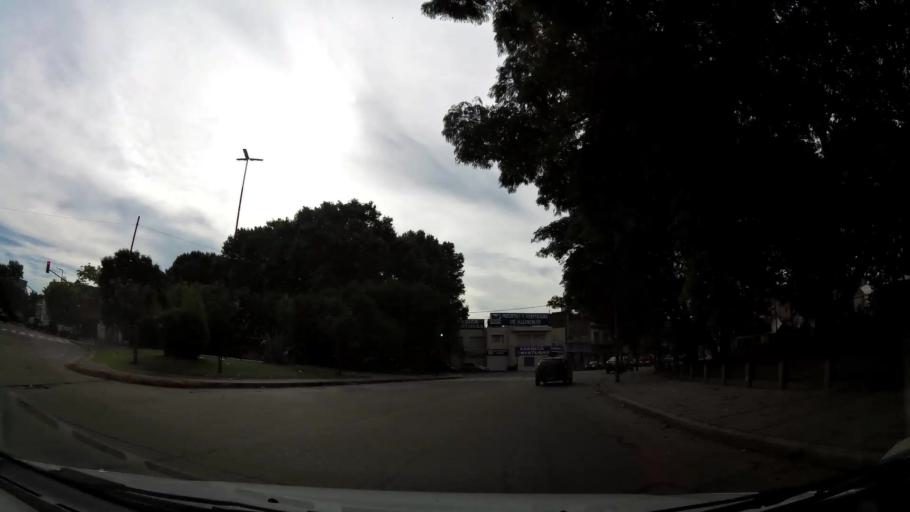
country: AR
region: Buenos Aires F.D.
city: Villa Santa Rita
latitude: -34.6426
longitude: -58.4621
